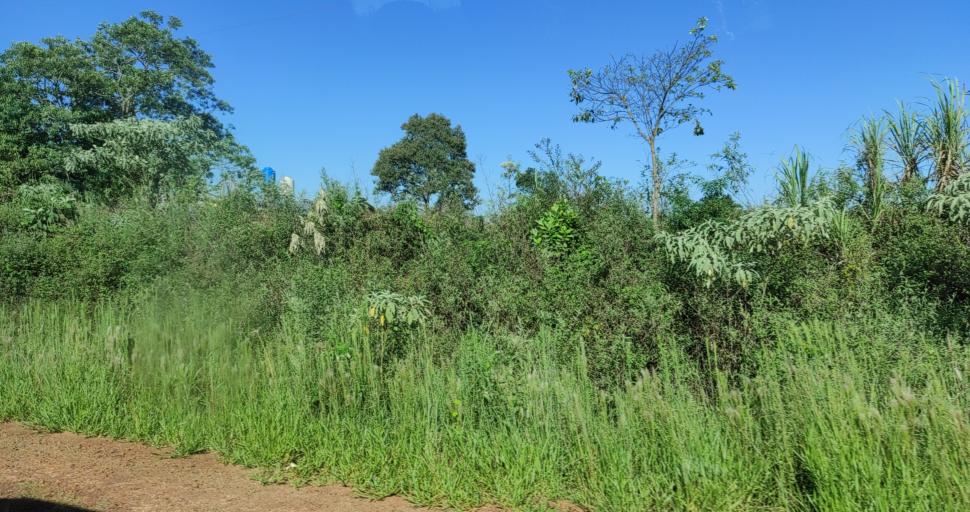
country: AR
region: Misiones
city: El Soberbio
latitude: -27.1891
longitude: -54.1064
